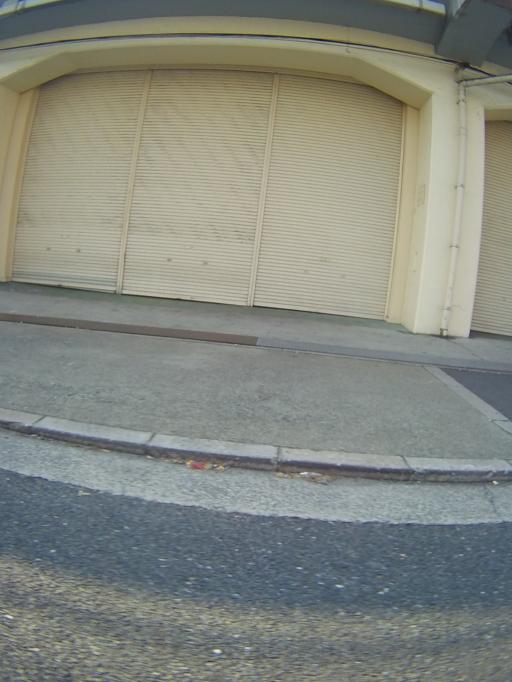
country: JP
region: Osaka
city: Osaka-shi
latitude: 34.6843
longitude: 135.4688
